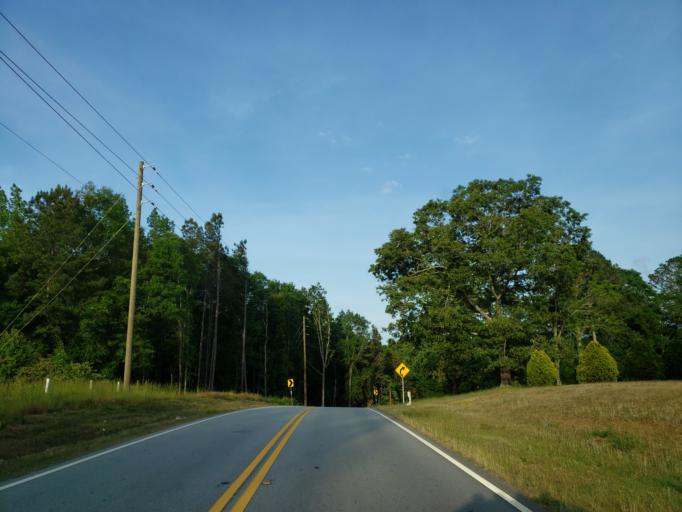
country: US
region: Georgia
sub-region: Carroll County
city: Carrollton
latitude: 33.5920
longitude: -85.1247
